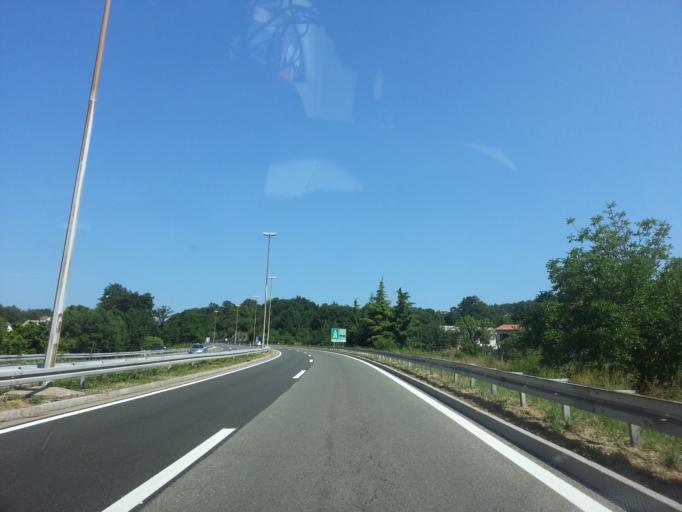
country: HR
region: Primorsko-Goranska
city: Matulji
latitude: 45.3704
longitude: 14.3263
